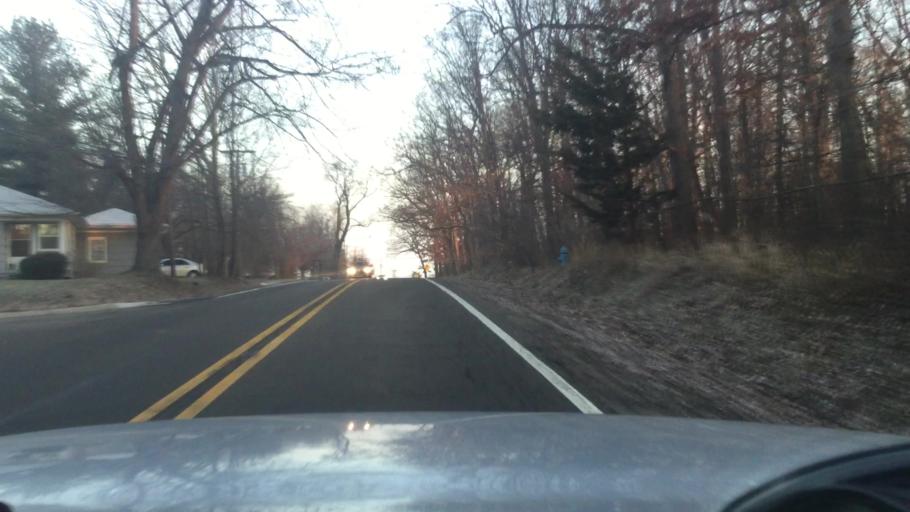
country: US
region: Michigan
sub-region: Oakland County
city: Waterford
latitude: 42.6720
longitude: -83.3571
